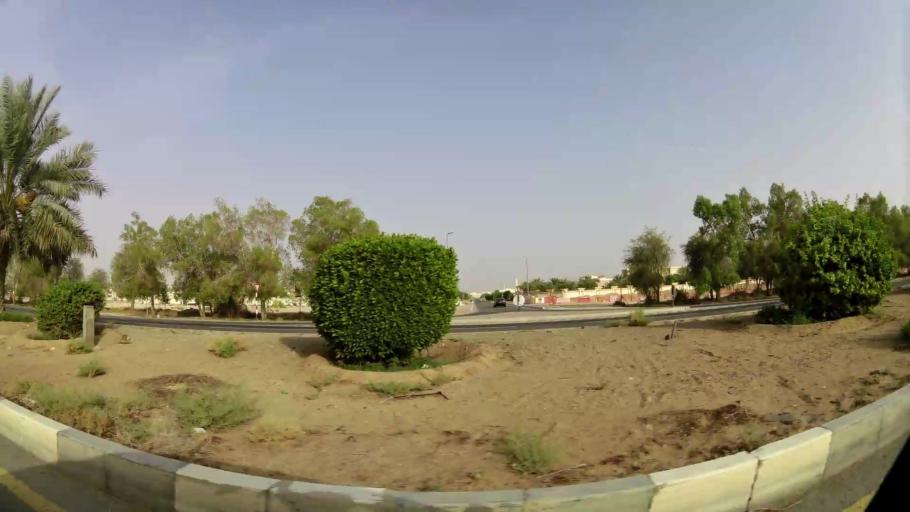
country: AE
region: Abu Dhabi
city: Al Ain
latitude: 24.1249
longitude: 55.7066
